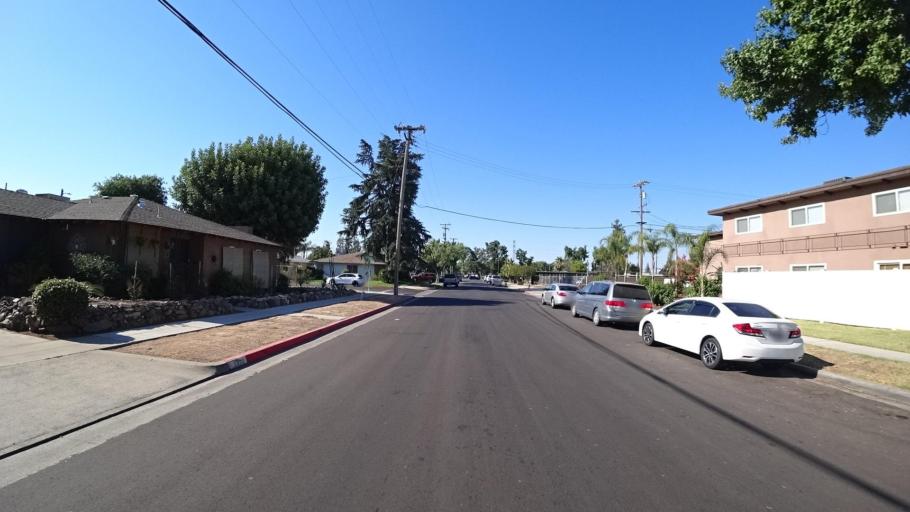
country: US
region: California
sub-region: Fresno County
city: Fresno
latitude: 36.7809
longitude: -119.7611
